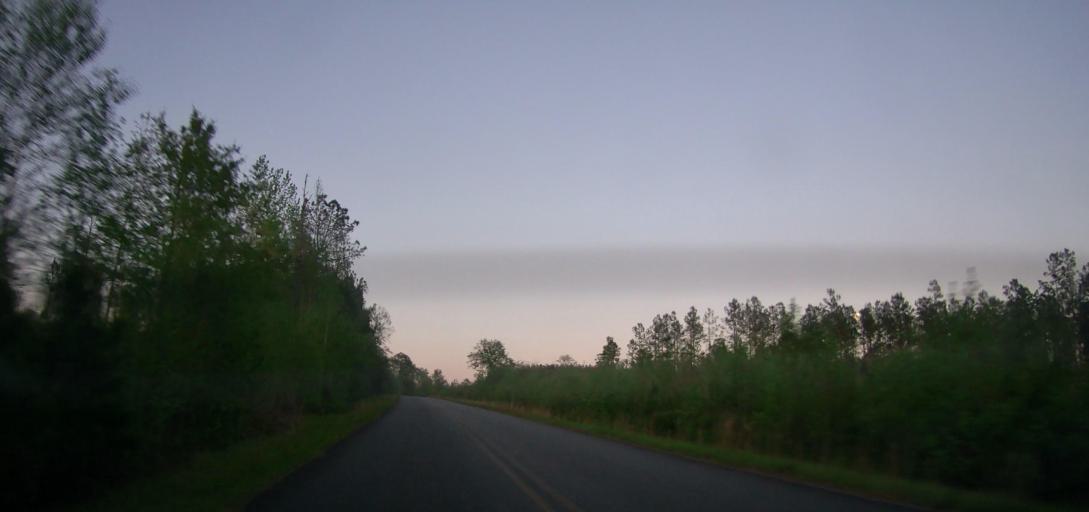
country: US
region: Georgia
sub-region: Marion County
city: Buena Vista
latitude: 32.2577
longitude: -84.5729
